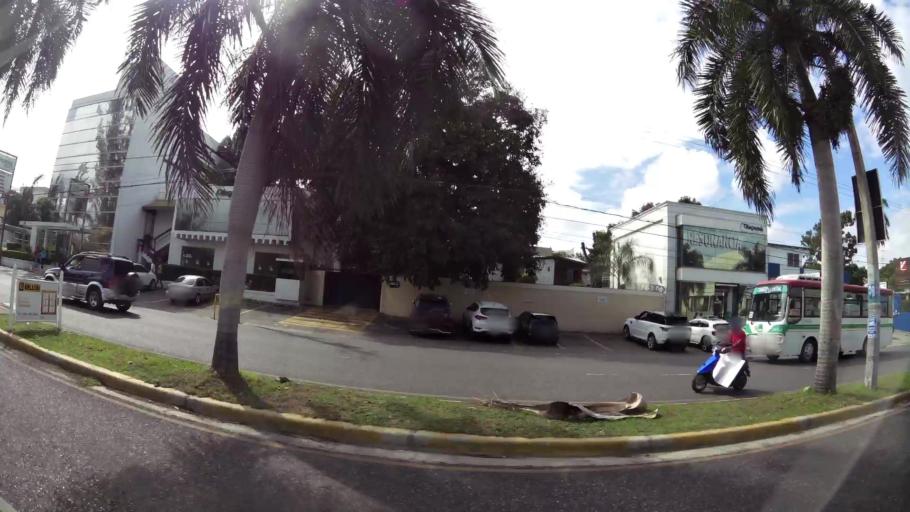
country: DO
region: Santiago
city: Santiago de los Caballeros
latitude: 19.4579
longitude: -70.6969
